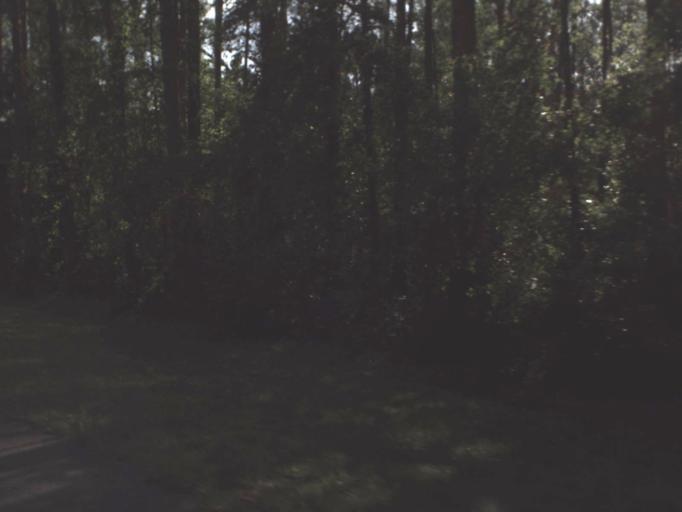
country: US
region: Florida
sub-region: Volusia County
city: Pierson
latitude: 29.2754
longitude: -81.3351
